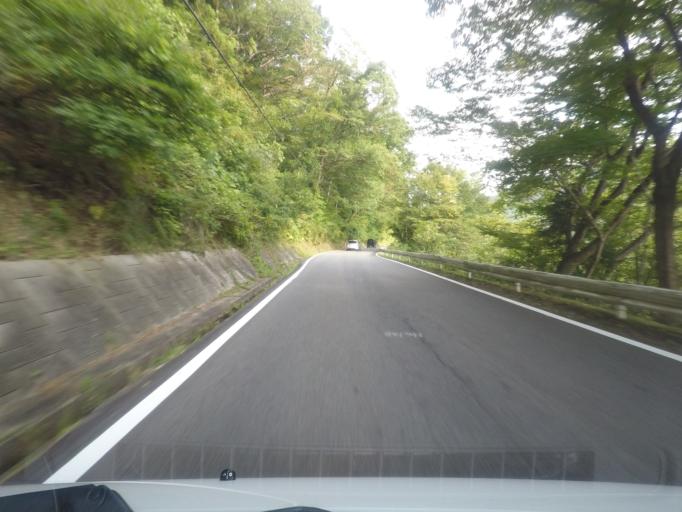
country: JP
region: Fukushima
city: Namie
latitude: 37.5629
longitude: 140.8126
